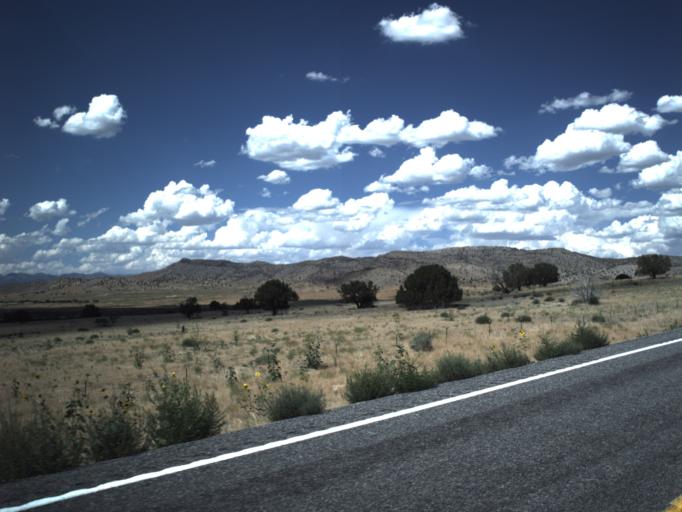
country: US
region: Utah
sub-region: Millard County
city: Delta
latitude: 39.6450
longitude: -112.3019
